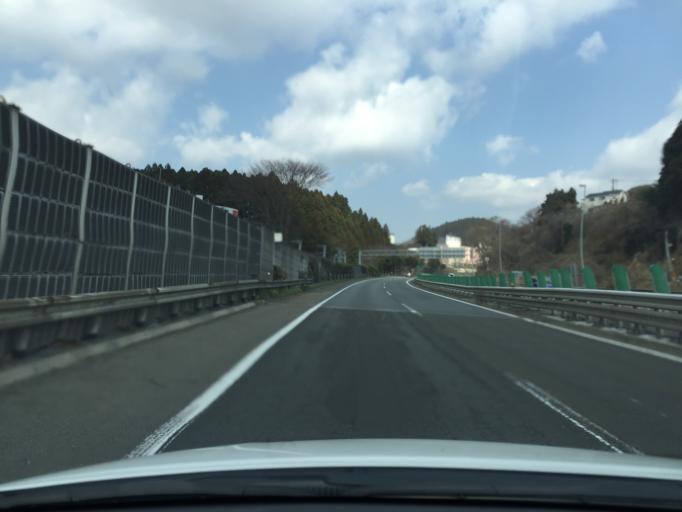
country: JP
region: Miyagi
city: Sendai
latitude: 38.2163
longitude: 140.8025
